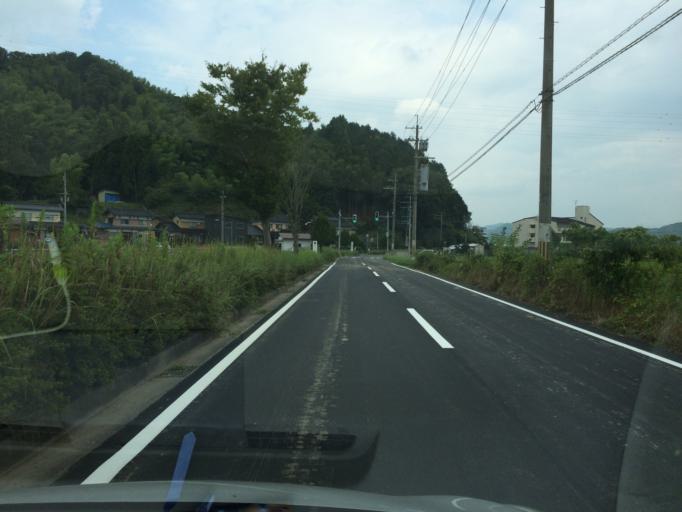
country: JP
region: Hyogo
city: Toyooka
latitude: 35.5112
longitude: 134.8143
